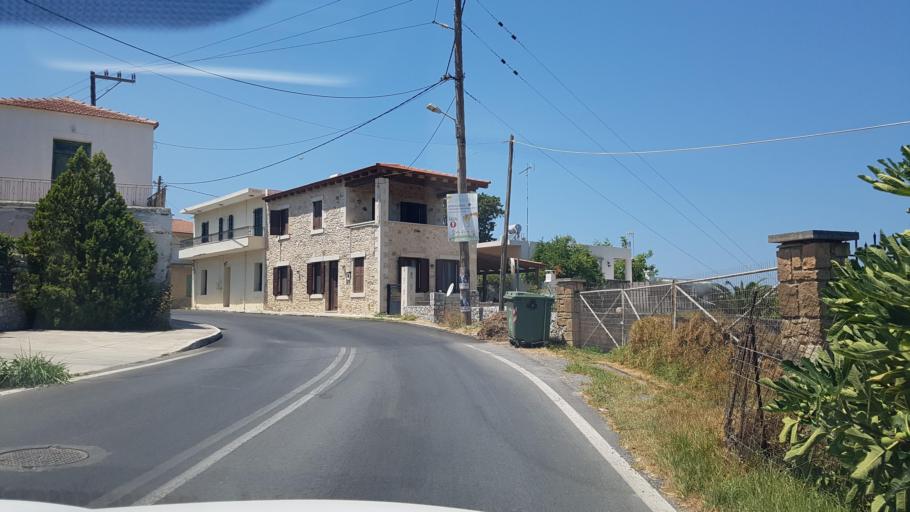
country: GR
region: Crete
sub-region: Nomos Rethymnis
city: Rethymno
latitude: 35.3573
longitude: 24.5621
